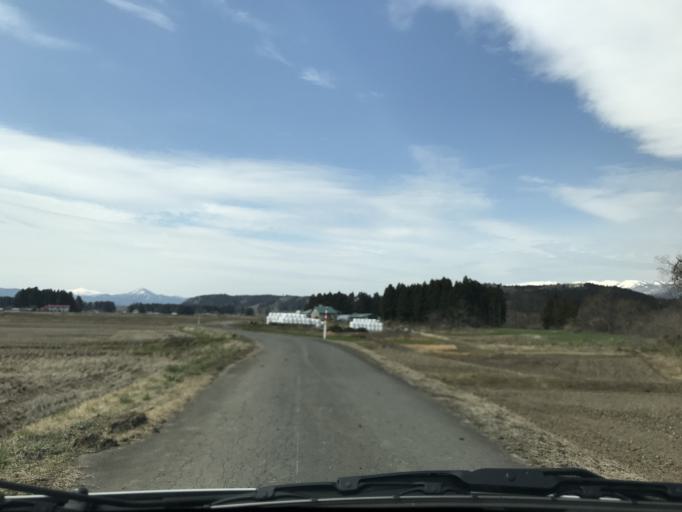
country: JP
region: Iwate
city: Mizusawa
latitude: 39.1481
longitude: 141.0546
